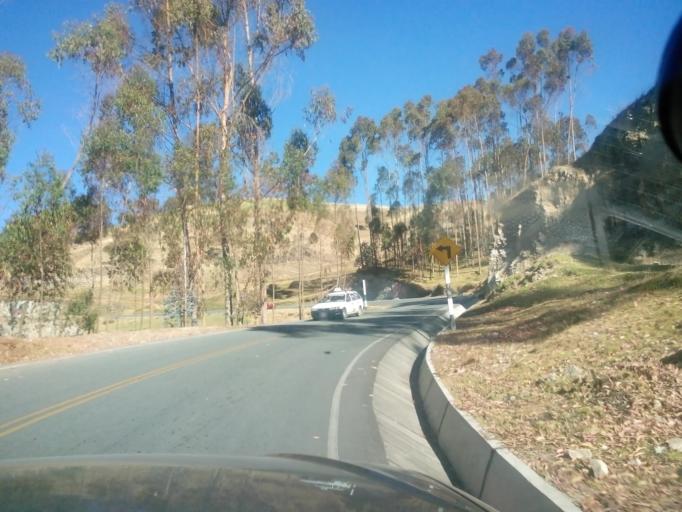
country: PE
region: Apurimac
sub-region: Provincia de Andahuaylas
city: Pacucha
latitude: -13.6555
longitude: -73.2934
